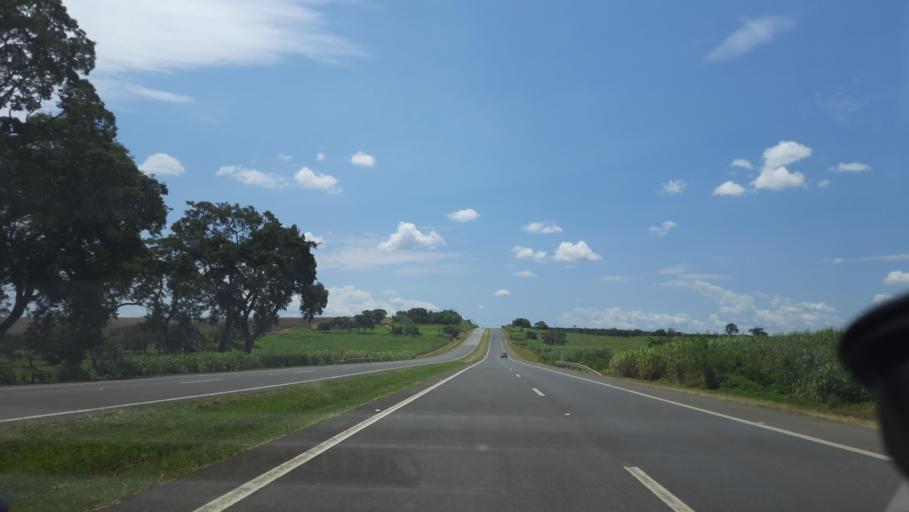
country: BR
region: Sao Paulo
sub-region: Mococa
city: Mococa
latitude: -21.6078
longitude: -47.0423
